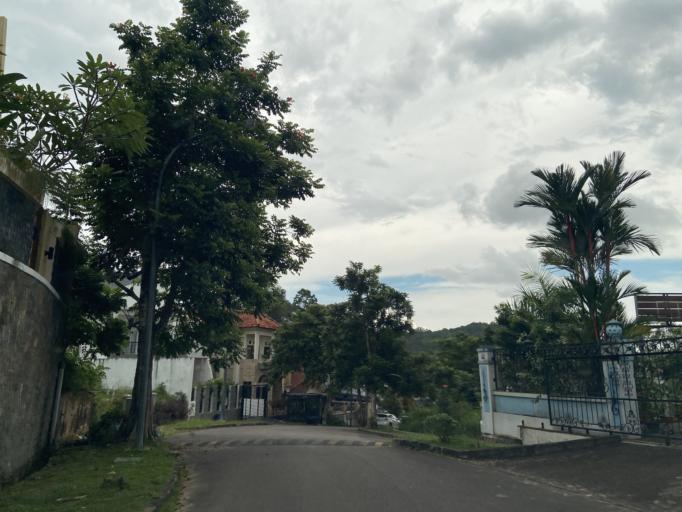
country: SG
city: Singapore
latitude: 1.1015
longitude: 104.0267
